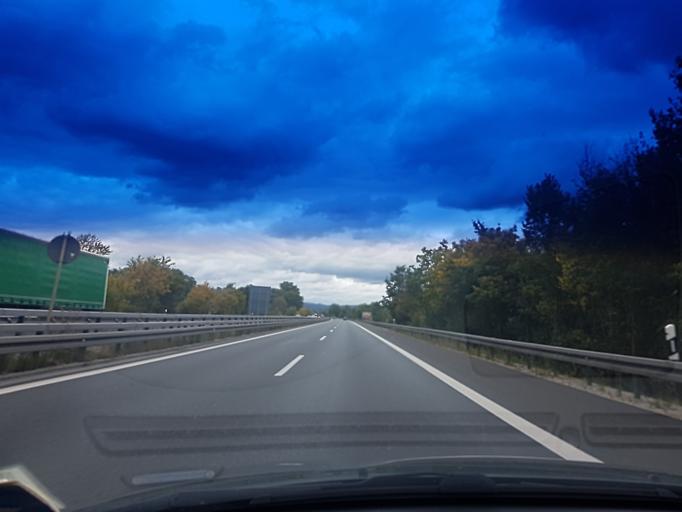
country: DE
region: Bavaria
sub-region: Upper Franconia
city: Gundelsheim
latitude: 49.9537
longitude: 10.9221
